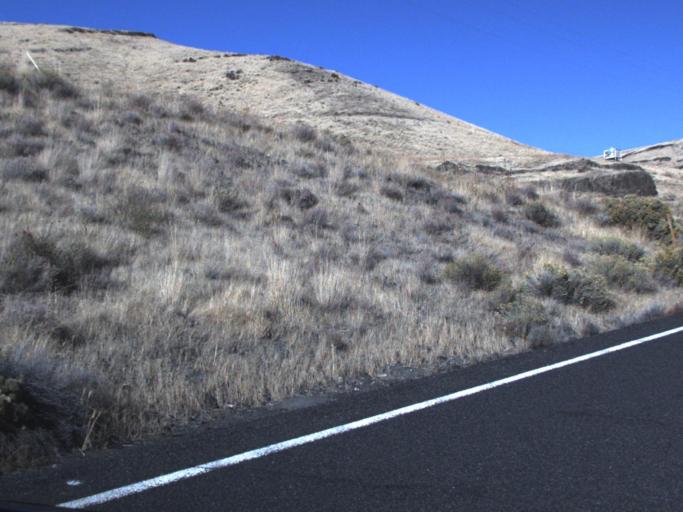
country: US
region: Washington
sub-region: Franklin County
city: Connell
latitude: 46.5690
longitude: -118.5391
